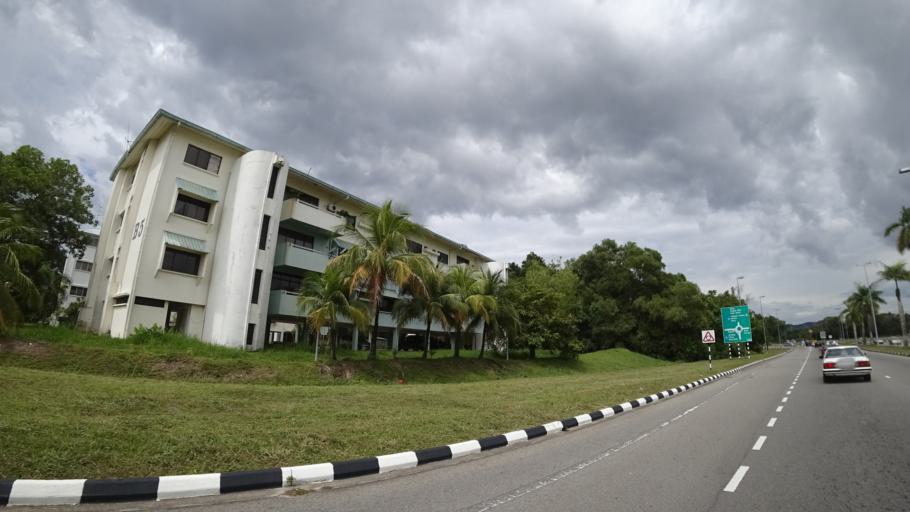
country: BN
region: Brunei and Muara
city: Bandar Seri Begawan
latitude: 4.8961
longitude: 114.9092
